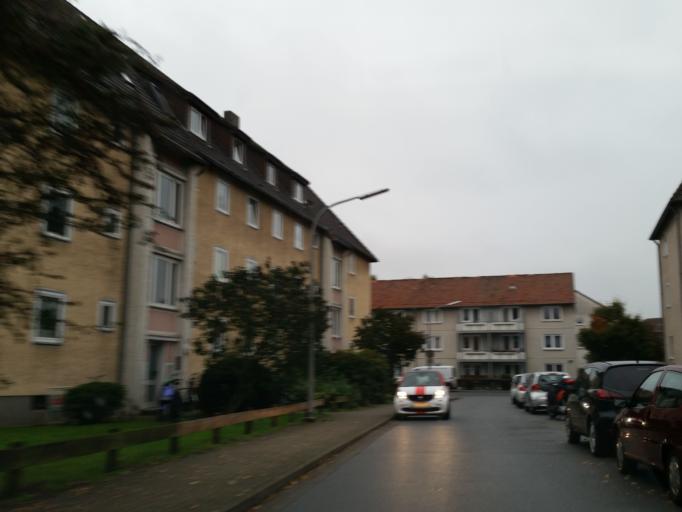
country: DE
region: Lower Saxony
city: Braunschweig
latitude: 52.2426
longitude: 10.5407
